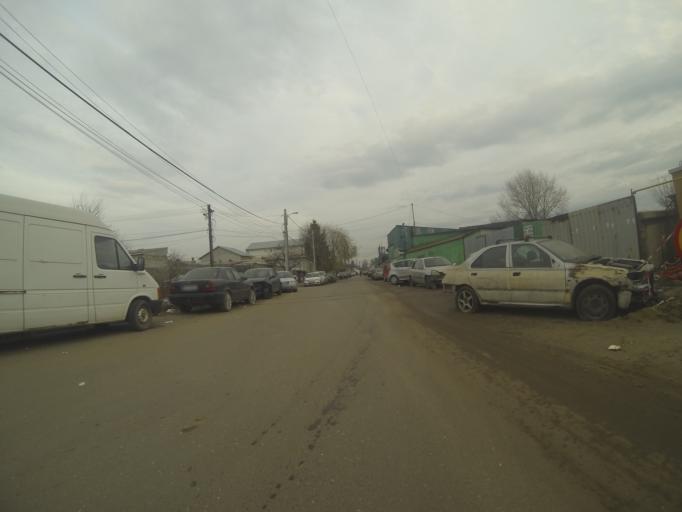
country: RO
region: Ilfov
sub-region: Comuna Jilava
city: Jilava
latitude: 44.3723
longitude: 26.0870
